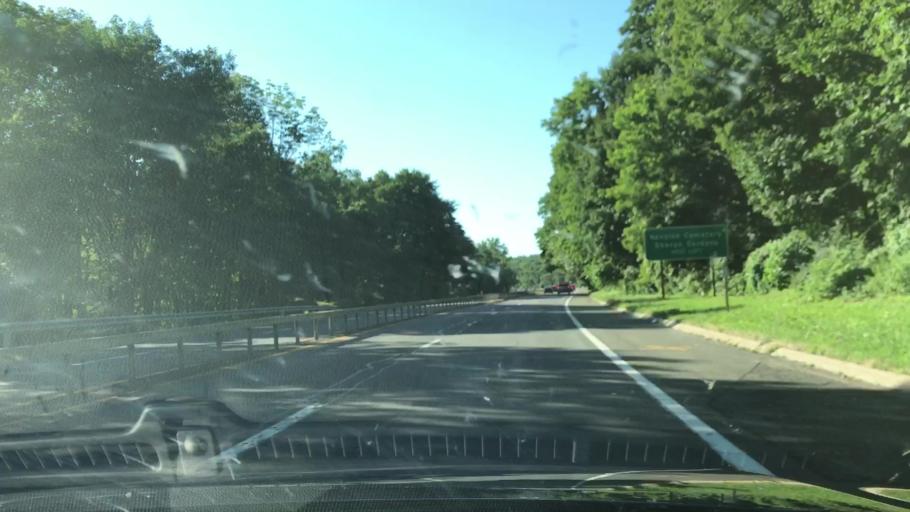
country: US
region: New York
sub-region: Westchester County
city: Valhalla
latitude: 41.0794
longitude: -73.7805
